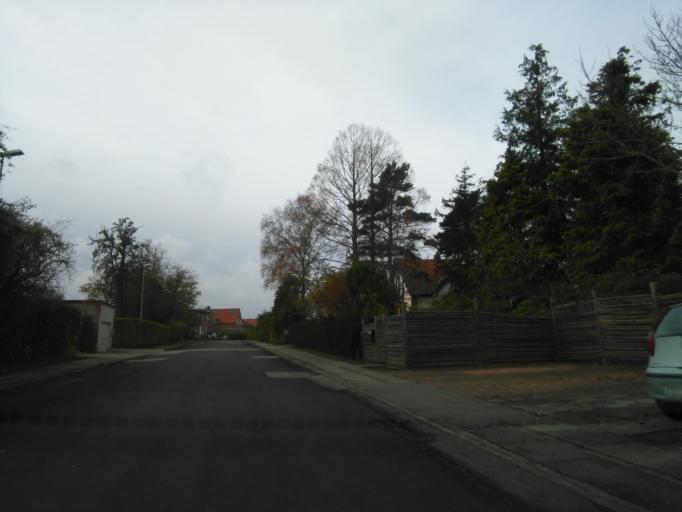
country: DK
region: Central Jutland
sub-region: Arhus Kommune
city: Arhus
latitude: 56.1892
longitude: 10.2360
